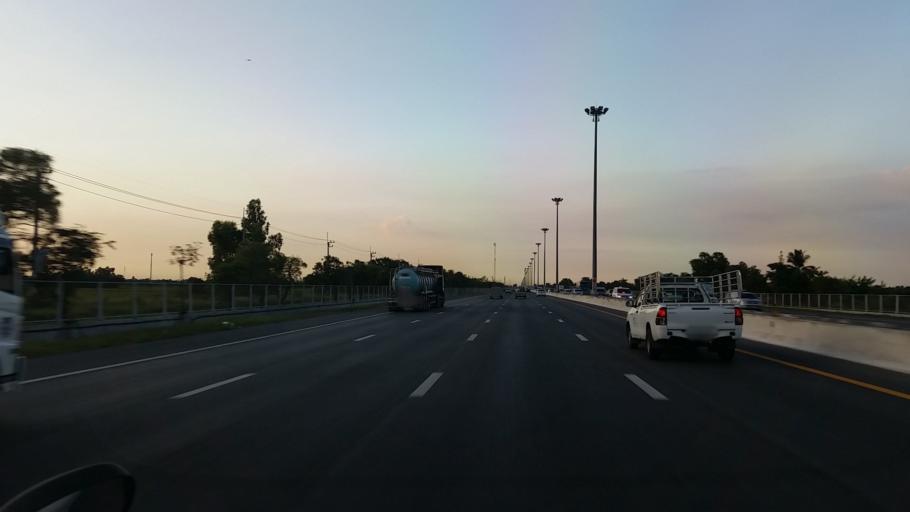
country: TH
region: Pathum Thani
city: Khlong Luang
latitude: 14.1123
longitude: 100.6800
